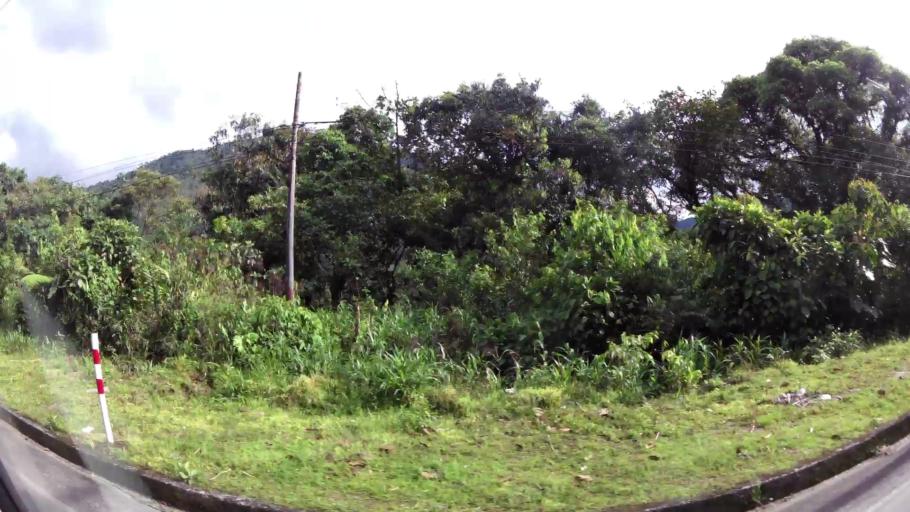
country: EC
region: Pastaza
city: Puyo
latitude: -1.4118
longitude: -78.1978
